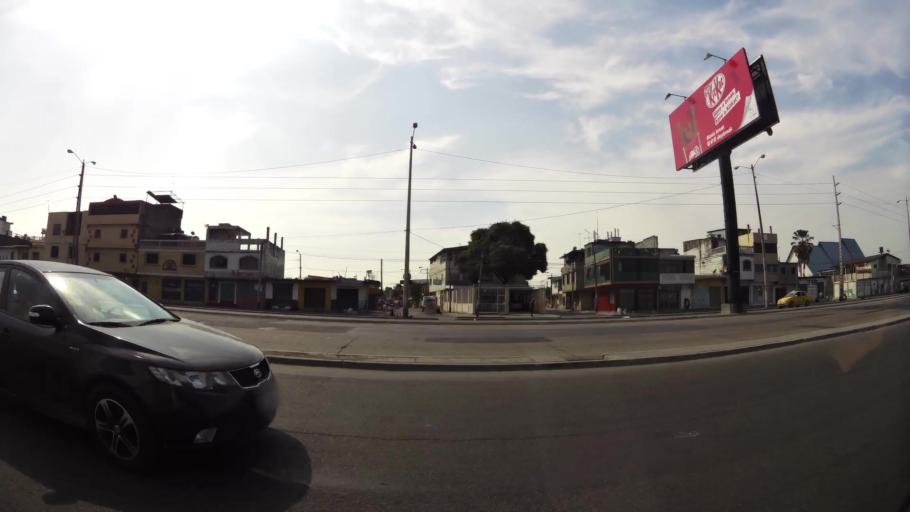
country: EC
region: Guayas
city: Guayaquil
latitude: -2.2555
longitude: -79.8942
